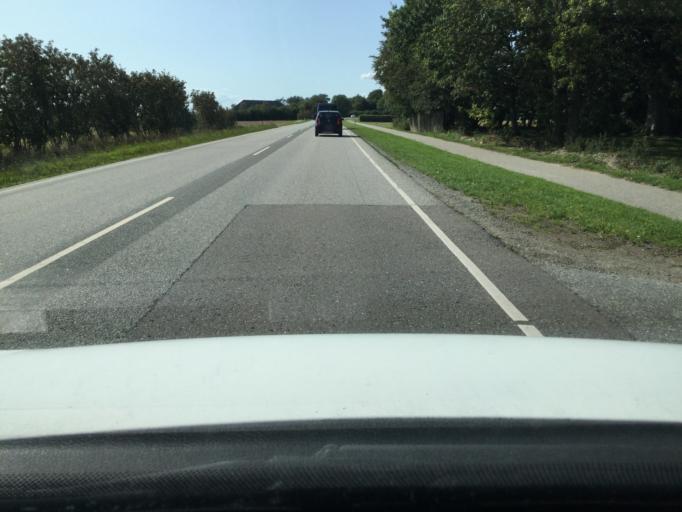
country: DK
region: Zealand
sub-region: Lolland Kommune
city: Nakskov
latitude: 54.8134
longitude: 11.1682
